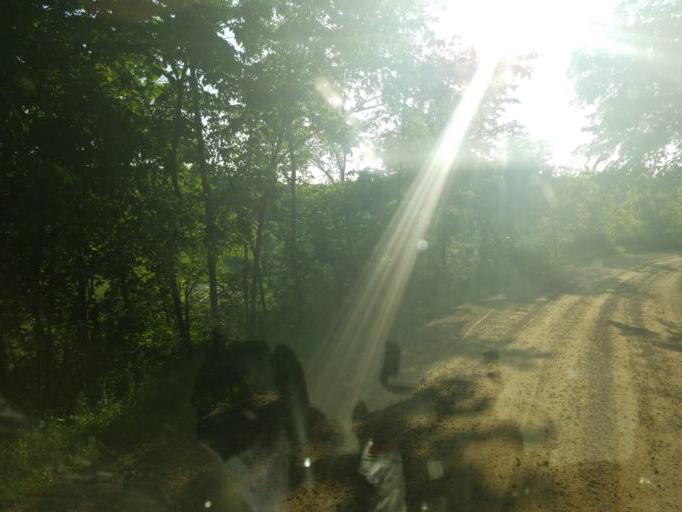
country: US
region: Wisconsin
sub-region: Vernon County
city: Hillsboro
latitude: 43.6247
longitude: -90.3351
